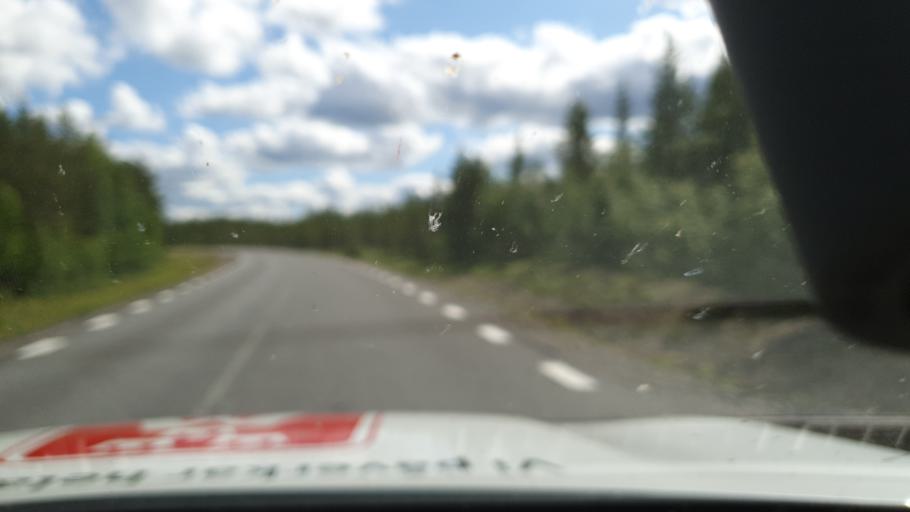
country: SE
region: Norrbotten
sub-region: Arjeplogs Kommun
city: Arjeplog
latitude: 65.5531
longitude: 18.1896
